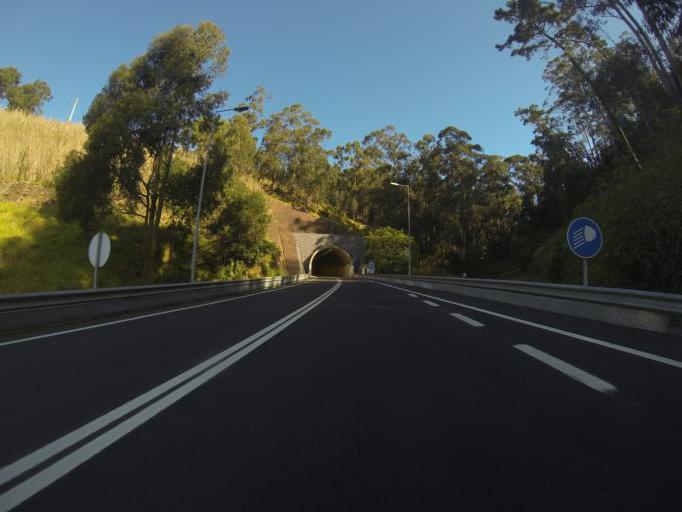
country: PT
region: Madeira
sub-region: Calheta
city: Estreito da Calheta
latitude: 32.7448
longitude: -17.1993
